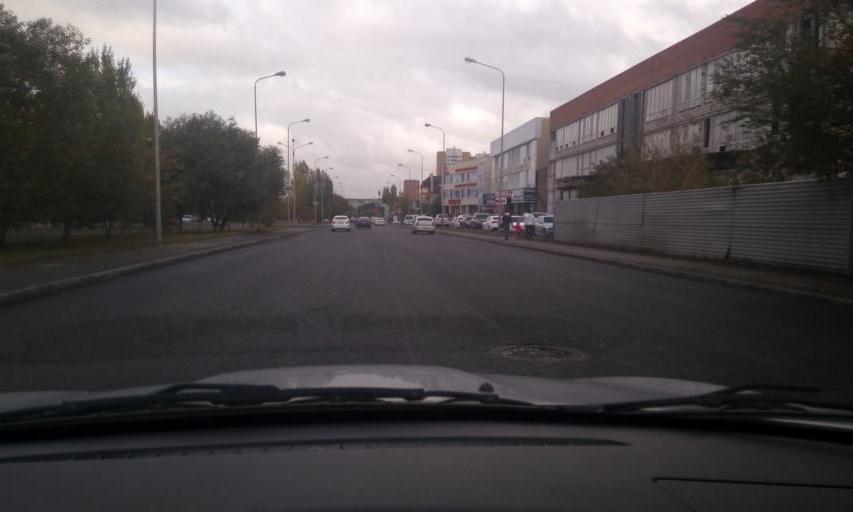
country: KZ
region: Astana Qalasy
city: Astana
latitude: 51.1650
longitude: 71.4671
